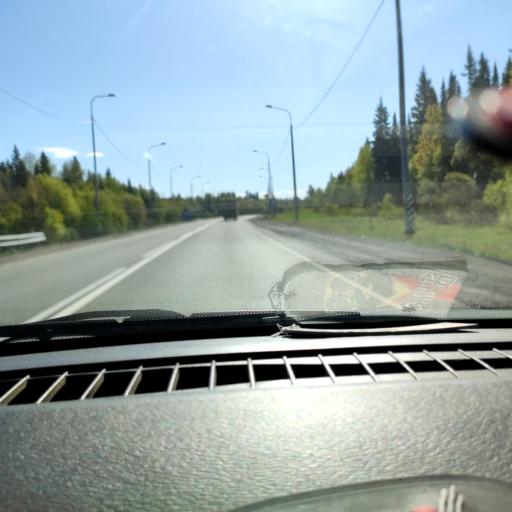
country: RU
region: Sverdlovsk
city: Arti
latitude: 56.7953
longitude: 58.4775
